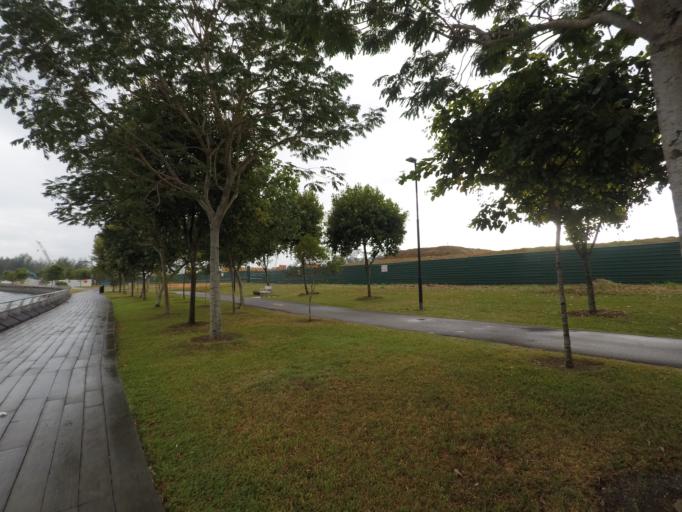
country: MY
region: Johor
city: Kampung Pasir Gudang Baru
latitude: 1.4181
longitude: 103.9140
